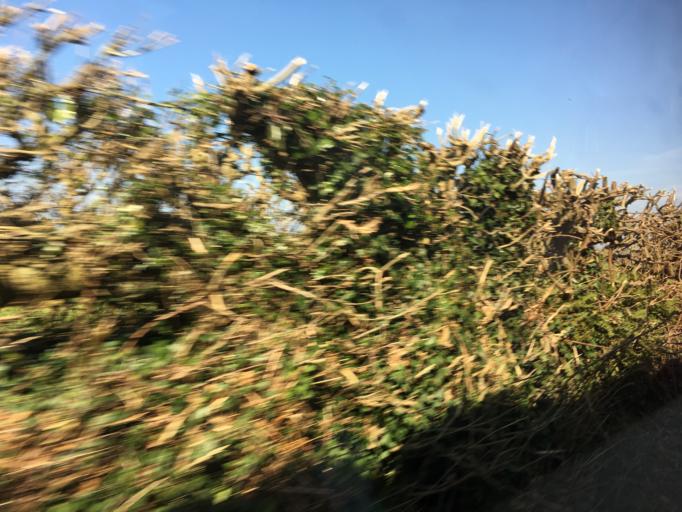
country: GB
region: Wales
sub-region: Gwynedd
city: Llanwnda
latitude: 53.0959
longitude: -4.2768
